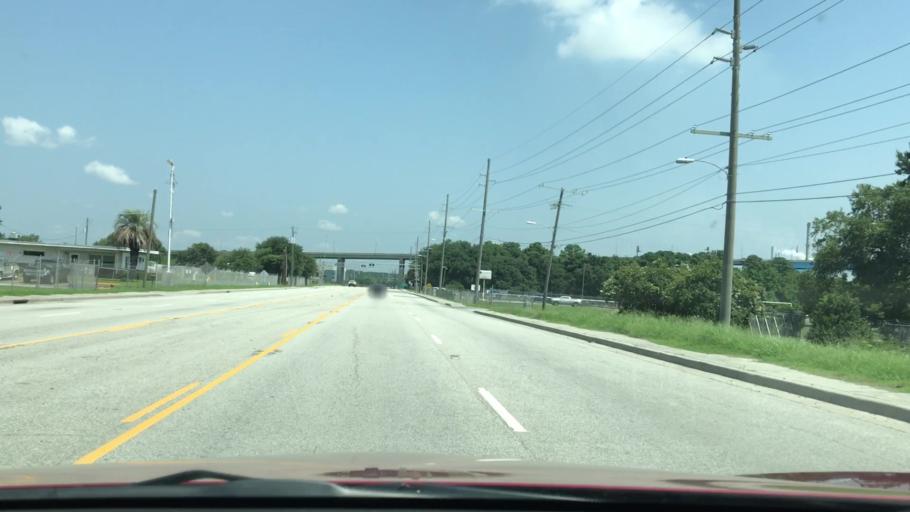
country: US
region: South Carolina
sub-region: Charleston County
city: North Charleston
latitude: 32.8879
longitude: -79.9728
